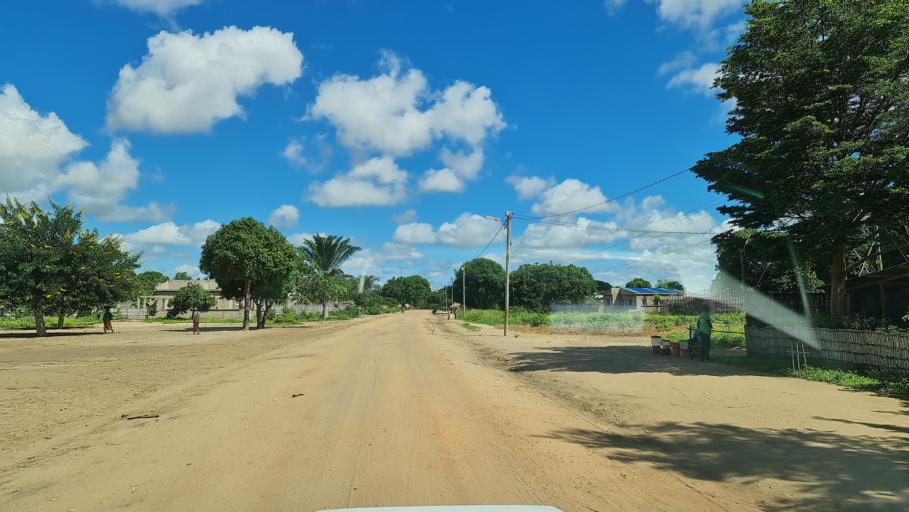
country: MZ
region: Nampula
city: Ilha de Mocambique
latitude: -15.5543
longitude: 40.4096
